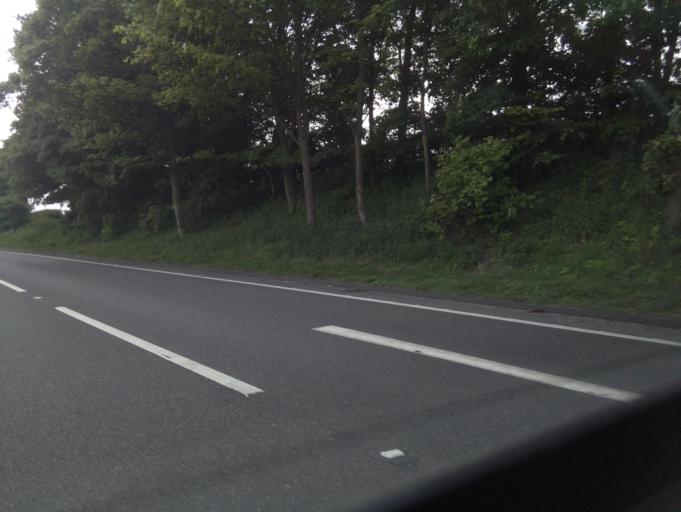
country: GB
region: England
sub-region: North Yorkshire
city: Thirsk
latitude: 54.3073
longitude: -1.3374
